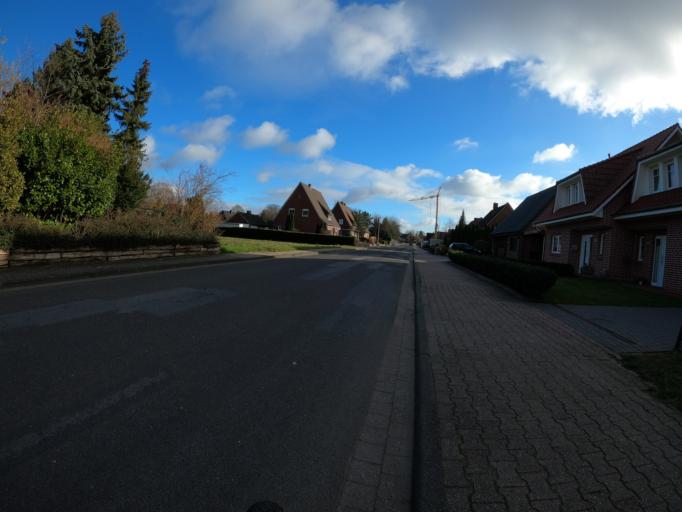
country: DE
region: Lower Saxony
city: Haselunne
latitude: 52.6712
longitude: 7.4735
